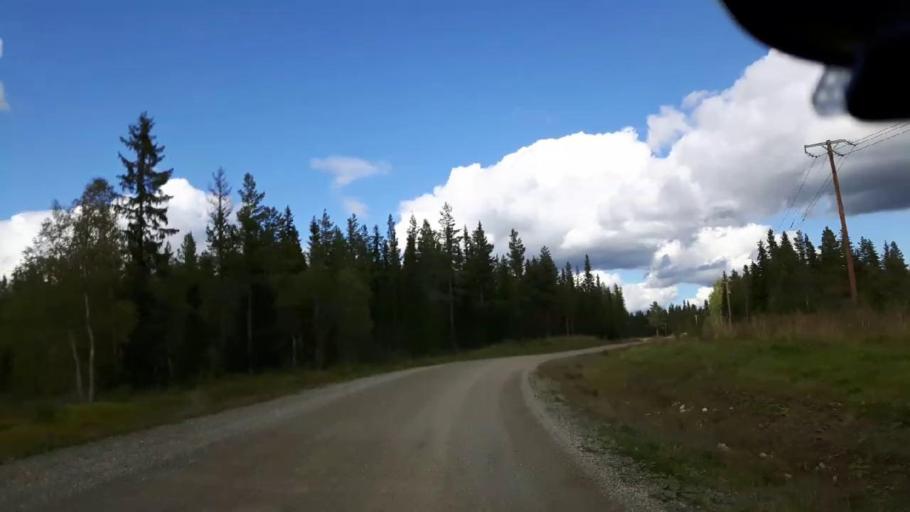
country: SE
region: Jaemtland
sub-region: Stroemsunds Kommun
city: Stroemsund
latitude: 63.3852
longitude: 15.5617
